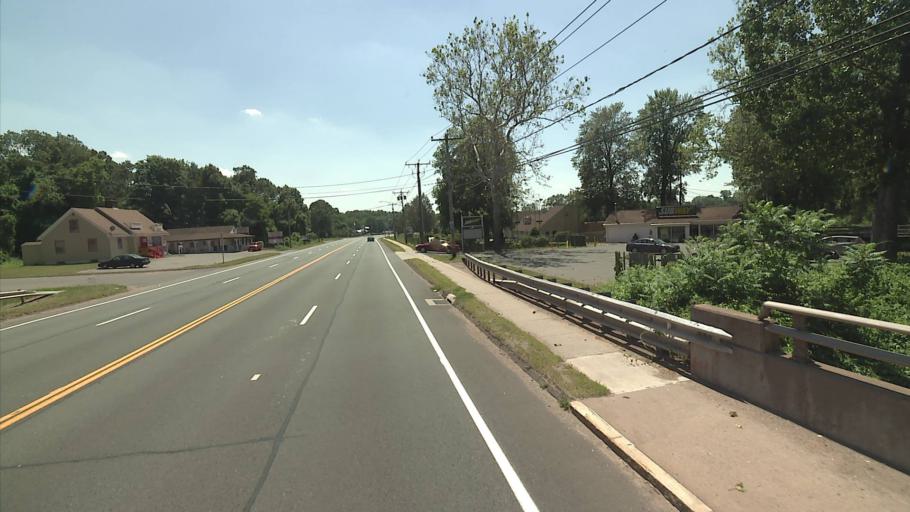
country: US
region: Connecticut
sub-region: Hartford County
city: Manchester
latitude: 41.8195
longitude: -72.5019
